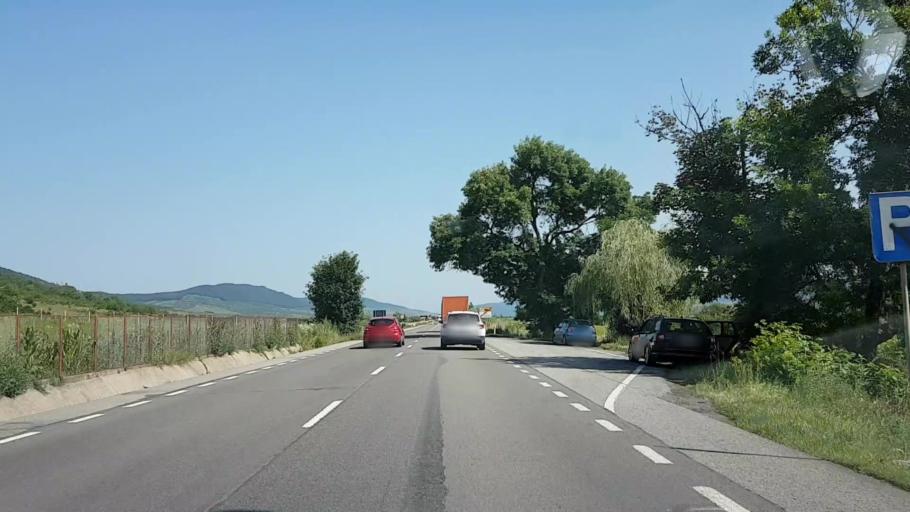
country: RO
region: Bistrita-Nasaud
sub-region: Comuna Sieu-Odorhei
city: Sieu-Odorhei
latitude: 47.1279
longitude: 24.3163
